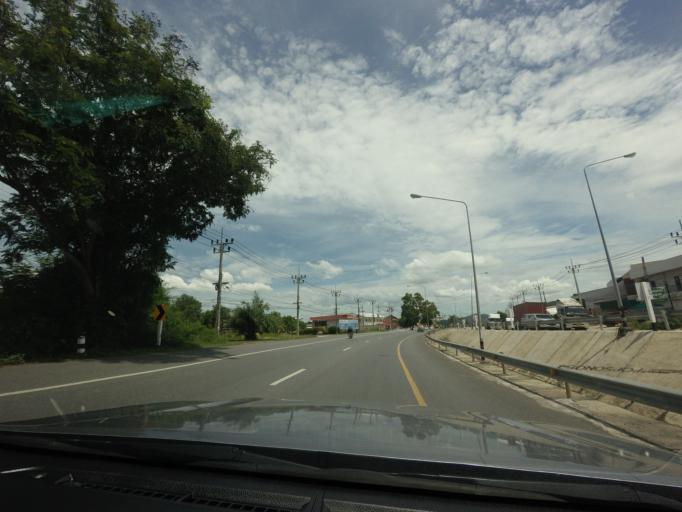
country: TH
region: Songkhla
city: Ban Mai
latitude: 7.2105
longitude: 100.5571
